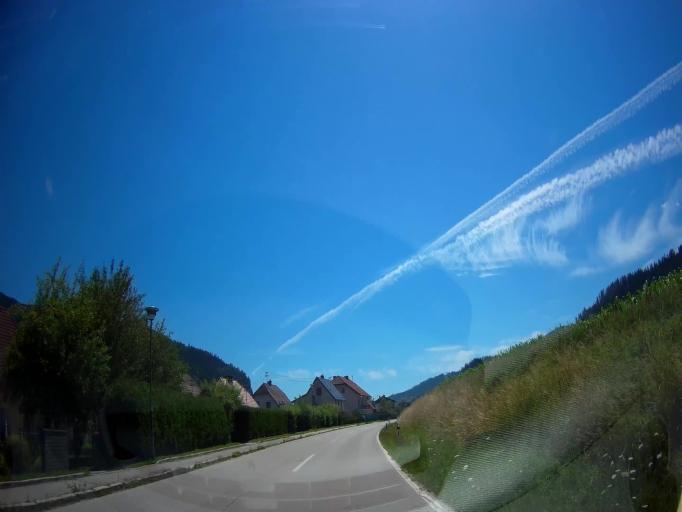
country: AT
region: Carinthia
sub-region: Politischer Bezirk Sankt Veit an der Glan
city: Micheldorf
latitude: 46.9117
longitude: 14.4333
